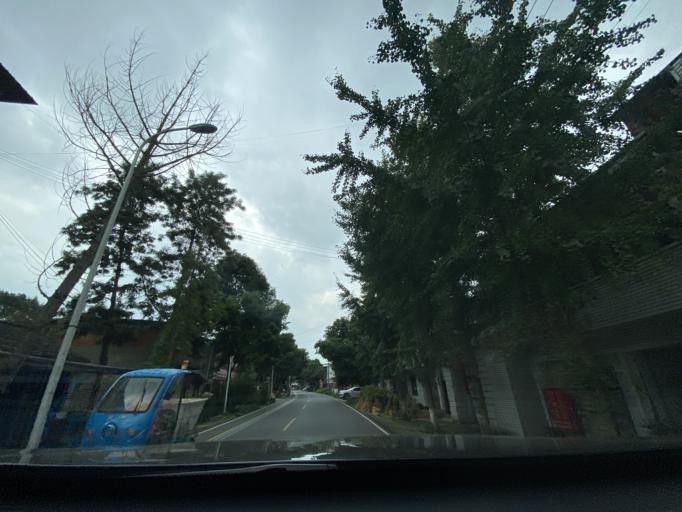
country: CN
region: Sichuan
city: Wujin
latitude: 30.4067
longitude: 103.9887
